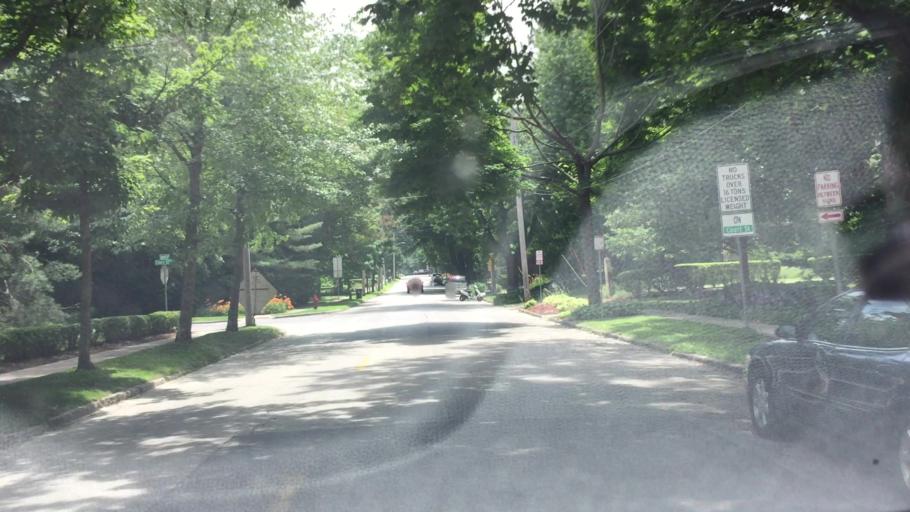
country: US
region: Iowa
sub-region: Johnson County
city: Iowa City
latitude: 41.6571
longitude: -91.5212
